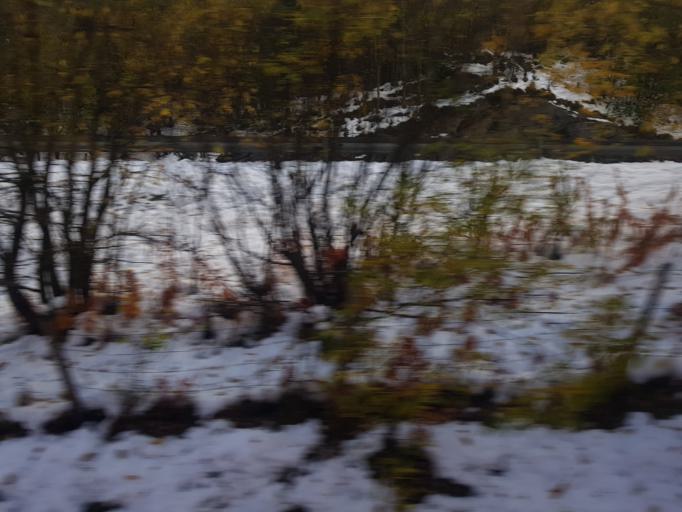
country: NO
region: Sor-Trondelag
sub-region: Oppdal
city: Oppdal
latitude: 62.4951
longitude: 9.5932
